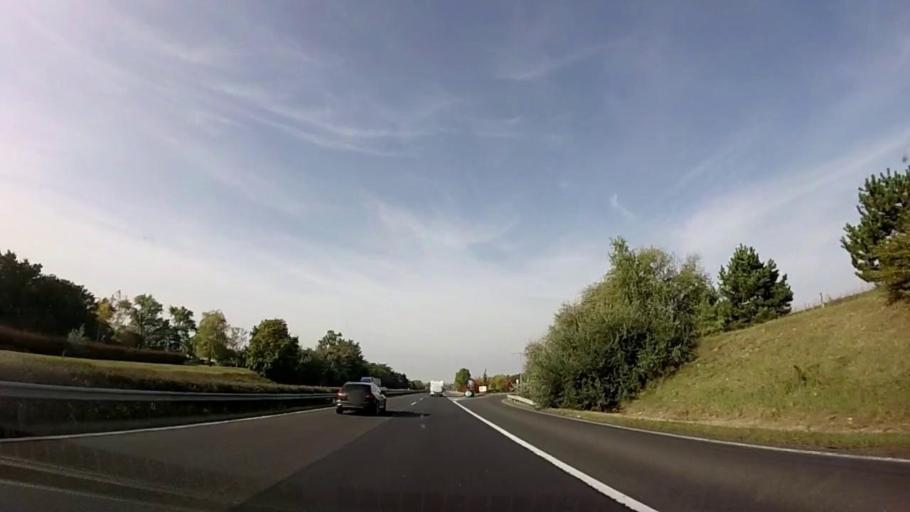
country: HU
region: Somogy
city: Siofok
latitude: 46.8837
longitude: 18.0129
